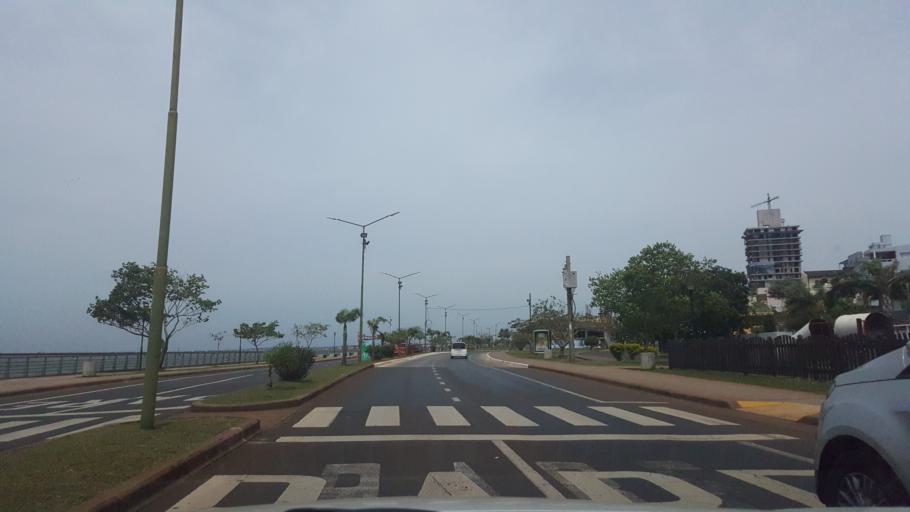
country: AR
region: Misiones
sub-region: Departamento de Capital
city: Posadas
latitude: -27.3656
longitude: -55.8847
